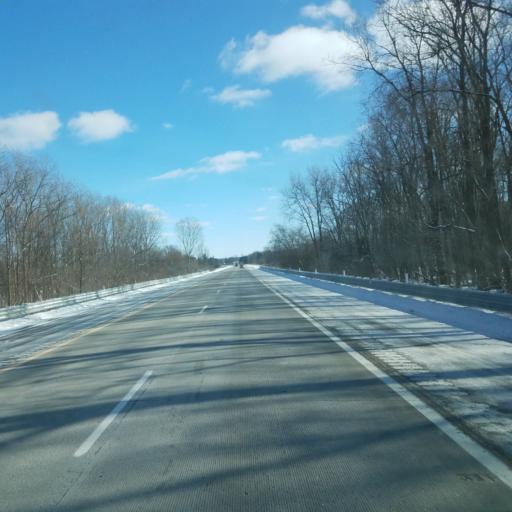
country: US
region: Michigan
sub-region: Ingham County
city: Okemos
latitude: 42.6756
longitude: -84.3990
